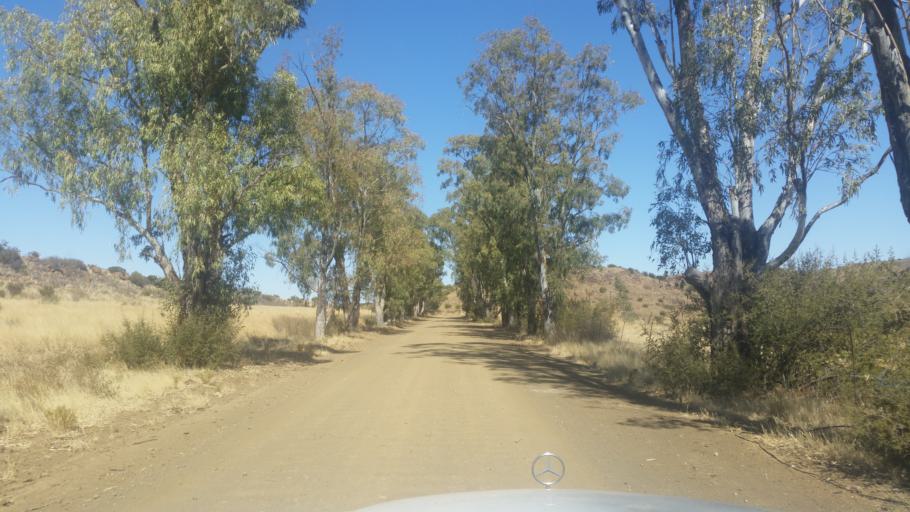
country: ZA
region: Orange Free State
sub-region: Xhariep District Municipality
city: Trompsburg
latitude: -30.4849
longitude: 25.9980
